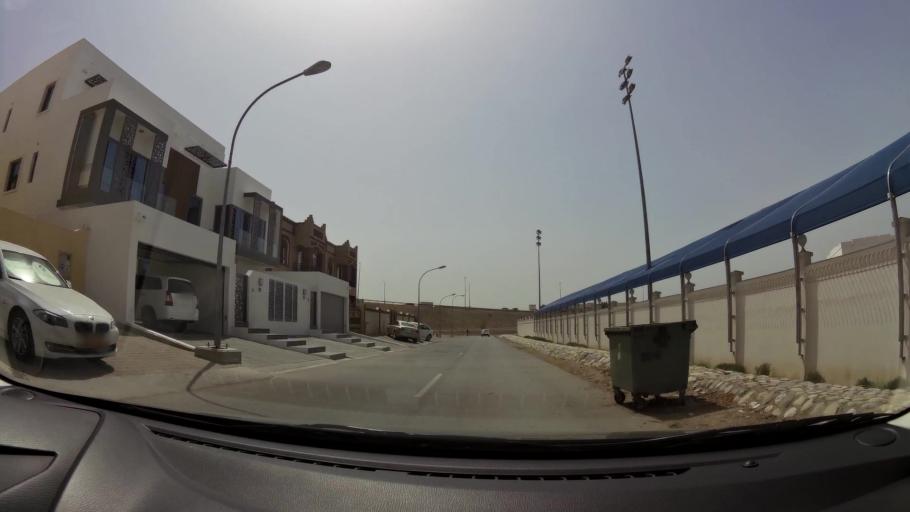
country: OM
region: Muhafazat Masqat
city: Bawshar
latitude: 23.5682
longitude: 58.3814
